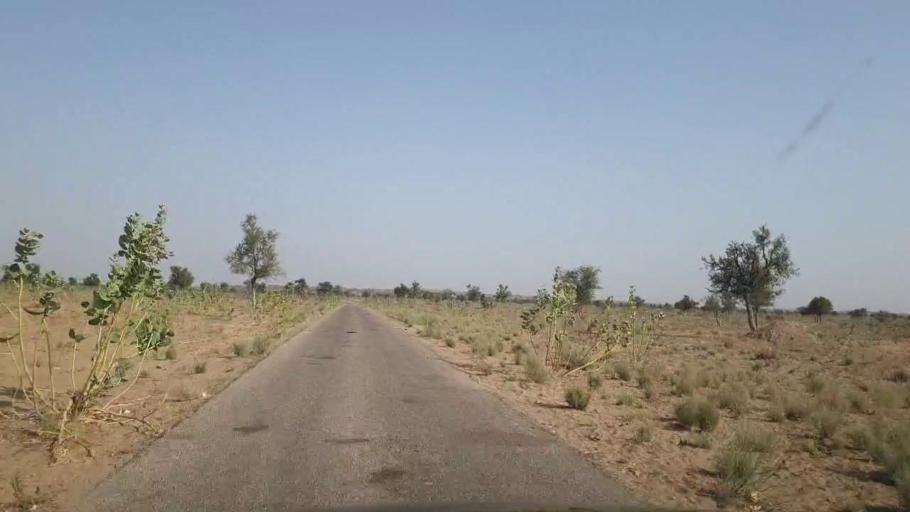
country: PK
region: Sindh
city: Islamkot
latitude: 25.1332
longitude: 70.4720
